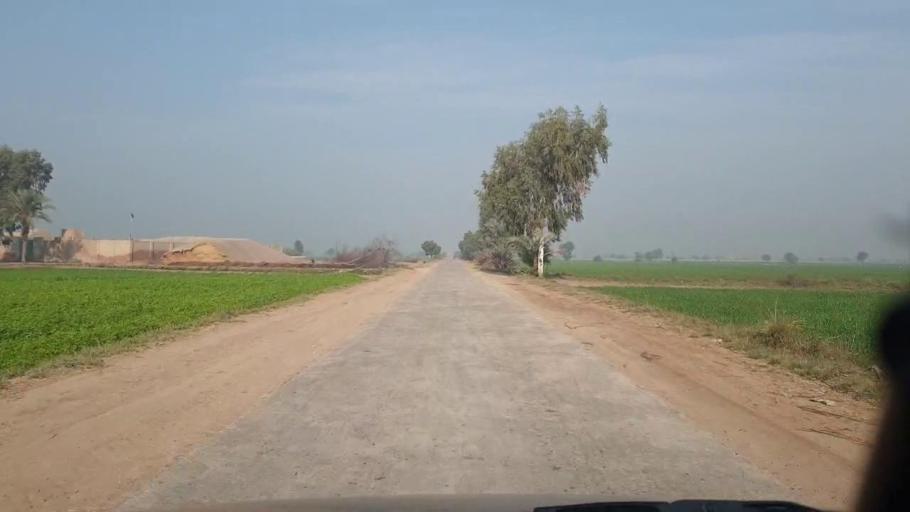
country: PK
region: Sindh
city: Shahdadpur
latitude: 25.9797
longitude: 68.5725
